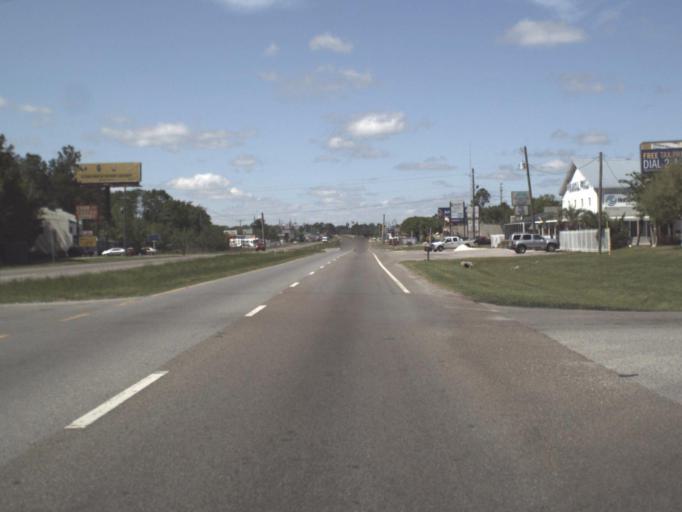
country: US
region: Florida
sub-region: Escambia County
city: Ensley
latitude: 30.5199
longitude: -87.2729
